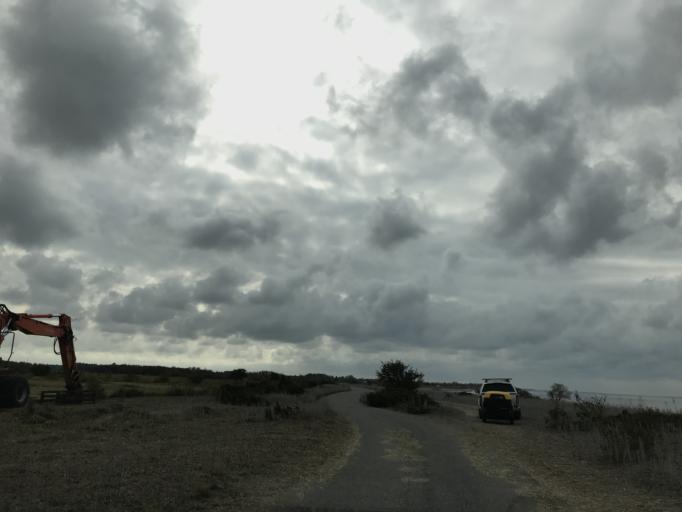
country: SE
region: Kalmar
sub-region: Borgholms Kommun
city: Borgholm
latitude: 57.0551
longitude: 16.8368
